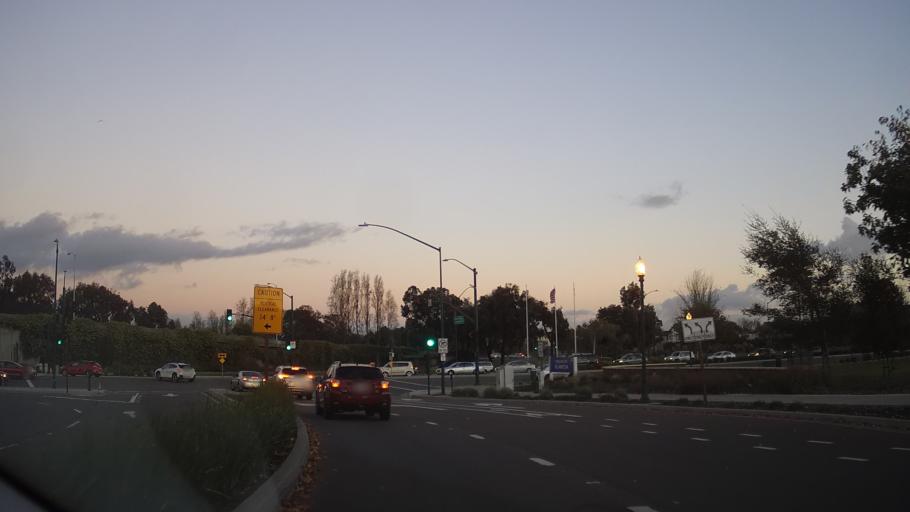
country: US
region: California
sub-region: Alameda County
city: Oakland
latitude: 37.7837
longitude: -122.2773
